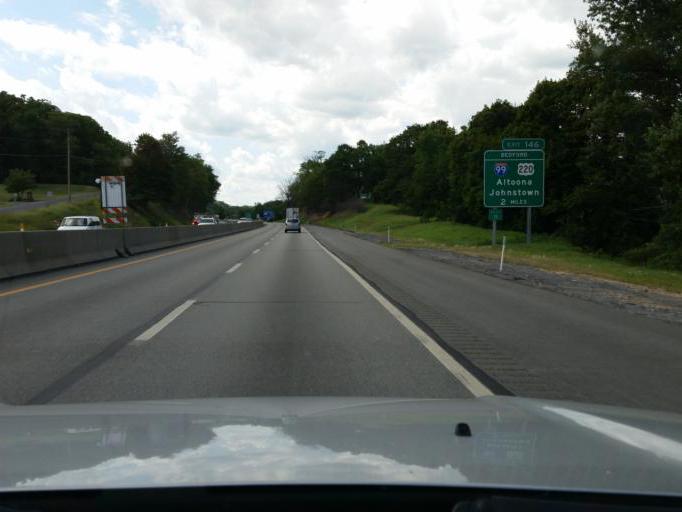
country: US
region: Pennsylvania
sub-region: Bedford County
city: Bedford
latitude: 40.0251
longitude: -78.4825
